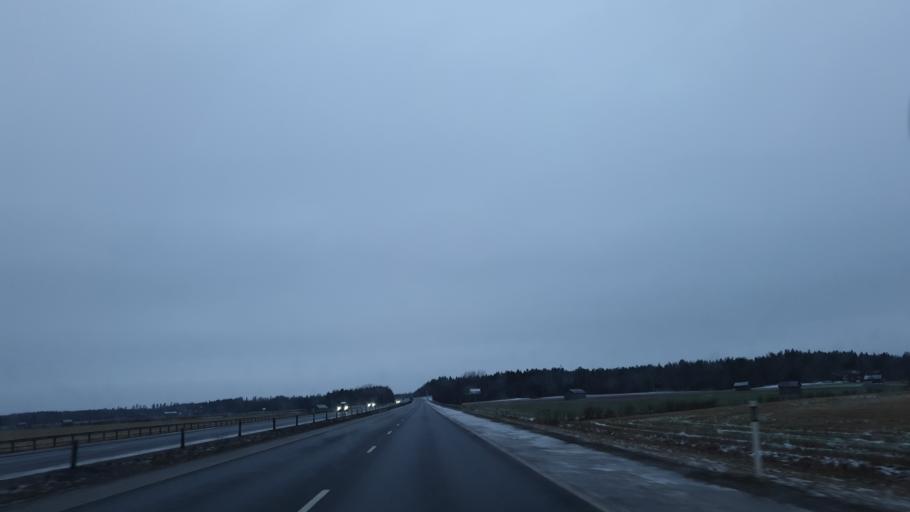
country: SE
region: Vaesterbotten
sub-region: Umea Kommun
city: Umea
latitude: 63.8001
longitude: 20.2328
